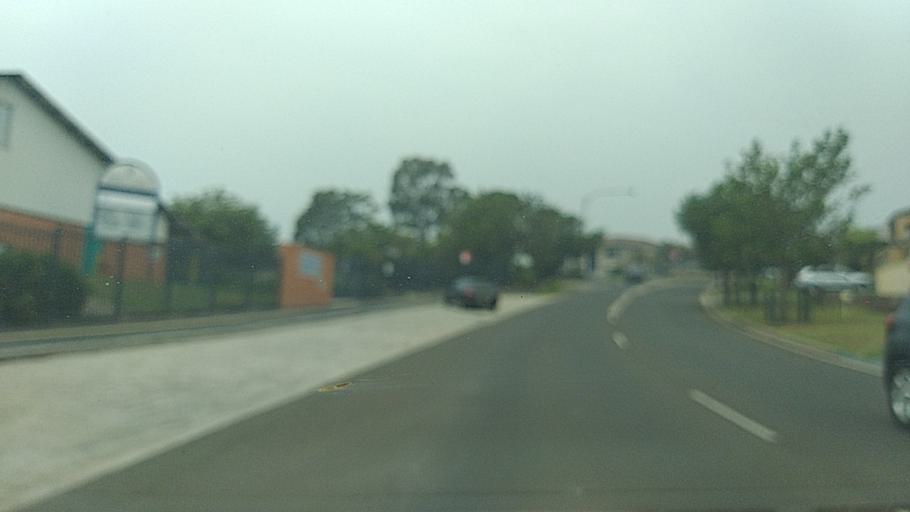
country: AU
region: New South Wales
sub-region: Shellharbour
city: Flinders
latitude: -34.5957
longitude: 150.8541
